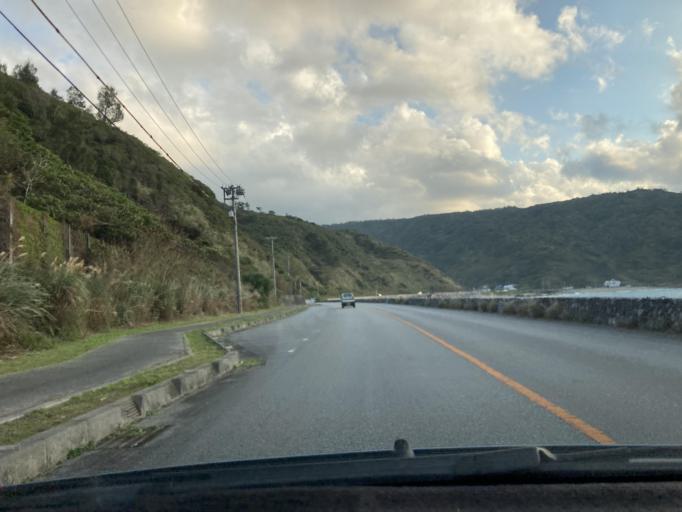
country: JP
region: Okinawa
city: Nago
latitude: 26.7725
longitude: 128.2046
